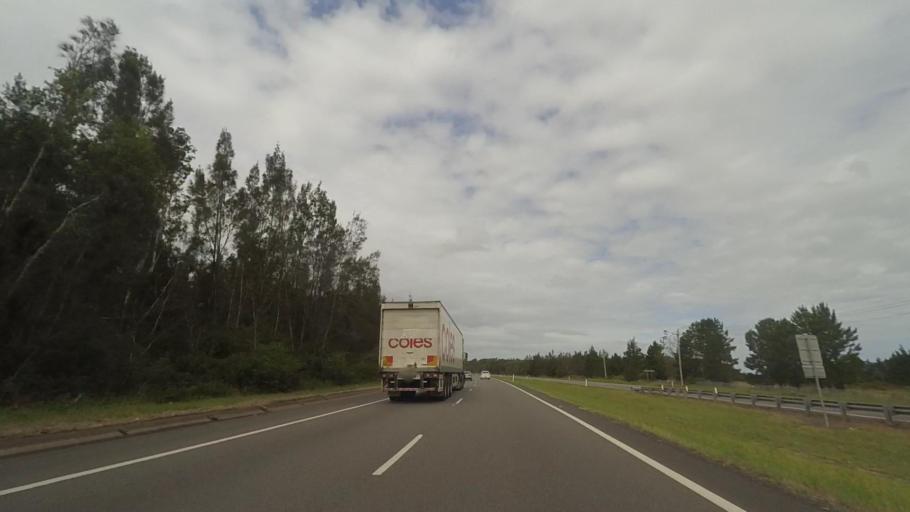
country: AU
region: New South Wales
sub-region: Port Stephens Shire
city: Raymond Terrace
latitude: -32.7781
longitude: 151.7515
